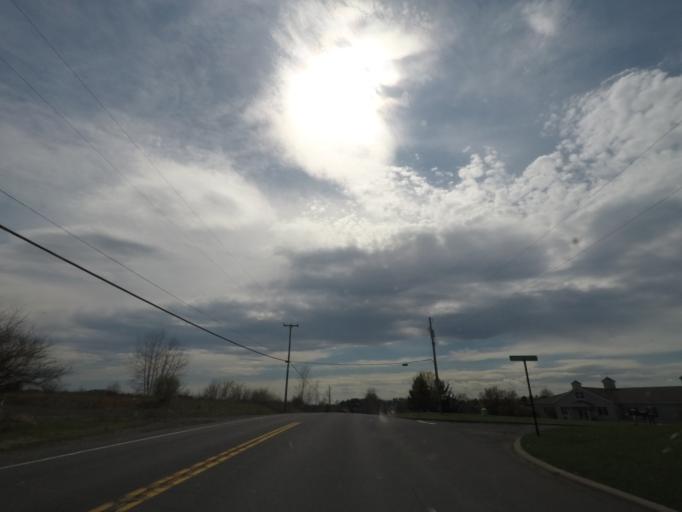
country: US
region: New York
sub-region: Columbia County
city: Stottville
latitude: 42.2807
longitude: -73.7089
